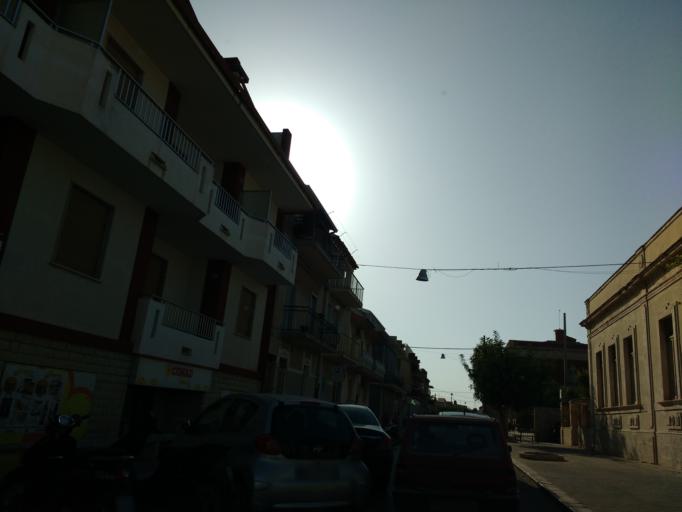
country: IT
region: Sicily
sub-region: Ragusa
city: Donnalucata
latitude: 36.7633
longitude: 14.6391
